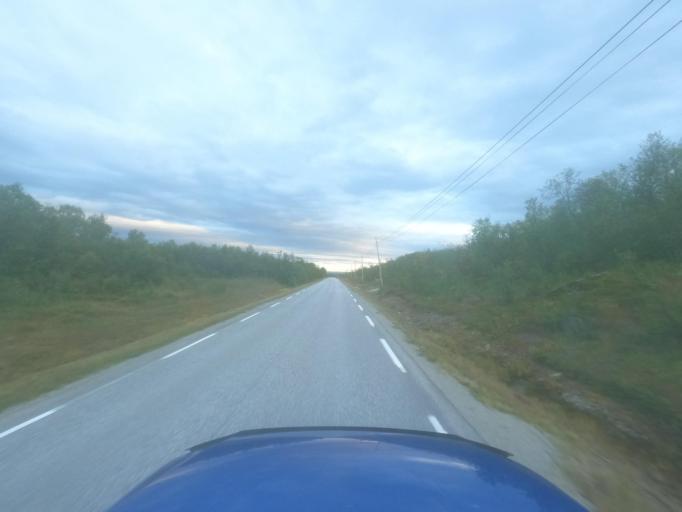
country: NO
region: Finnmark Fylke
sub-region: Porsanger
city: Lakselv
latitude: 70.1999
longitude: 24.9130
